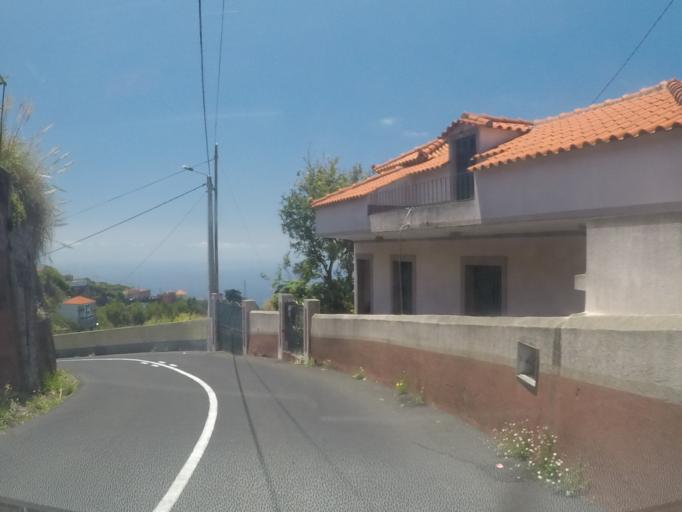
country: PT
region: Madeira
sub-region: Camara de Lobos
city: Curral das Freiras
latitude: 32.6847
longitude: -16.9928
